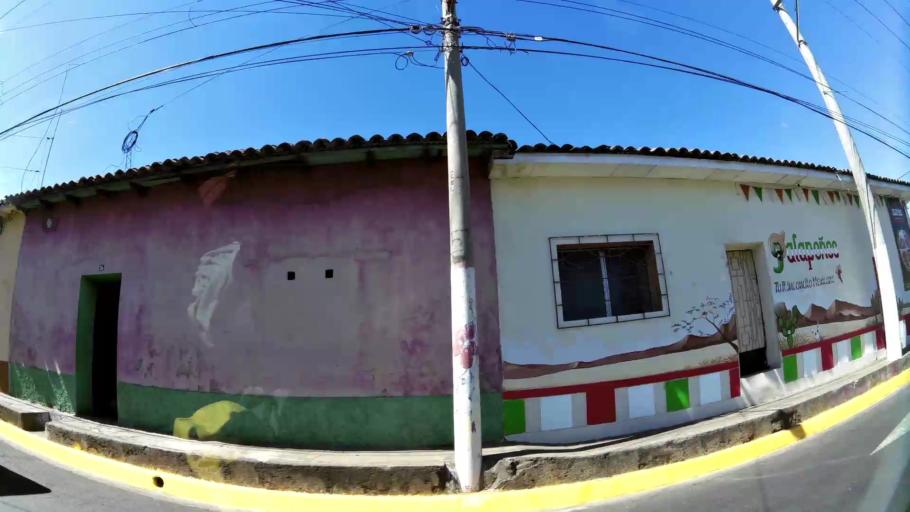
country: SV
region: La Libertad
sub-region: Distrito de Quezaltepeque
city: Quezaltepeque
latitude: 13.8324
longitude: -89.2750
